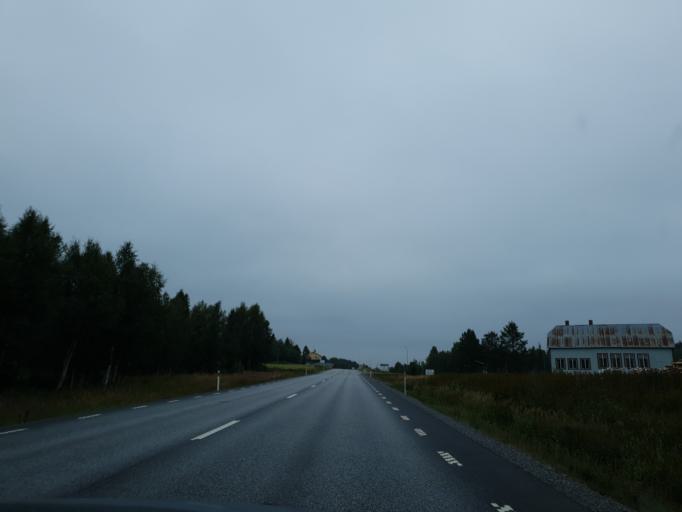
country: SE
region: Vaesterbotten
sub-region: Robertsfors Kommun
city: Robertsfors
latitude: 64.2276
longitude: 21.0162
